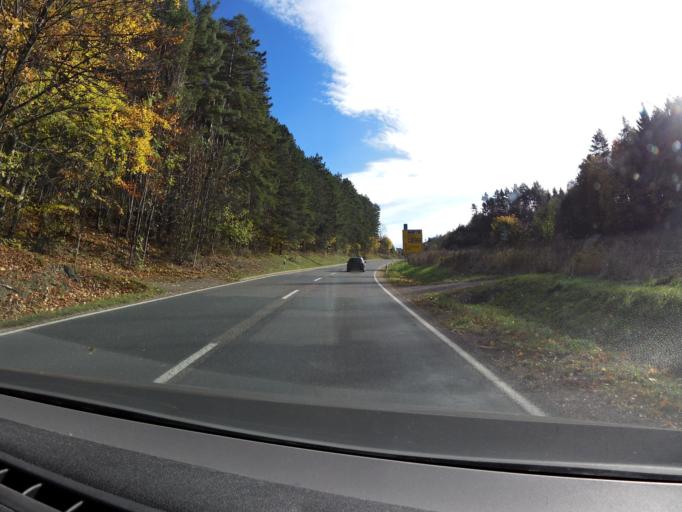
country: DE
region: Thuringia
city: Geschwenda
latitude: 50.7419
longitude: 10.8214
